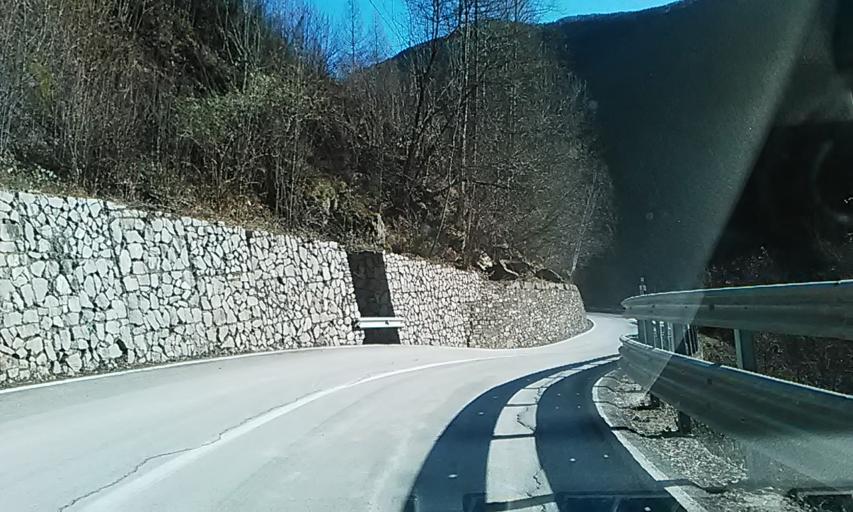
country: IT
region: Piedmont
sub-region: Provincia di Vercelli
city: Boccioleto
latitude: 45.8292
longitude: 8.1001
